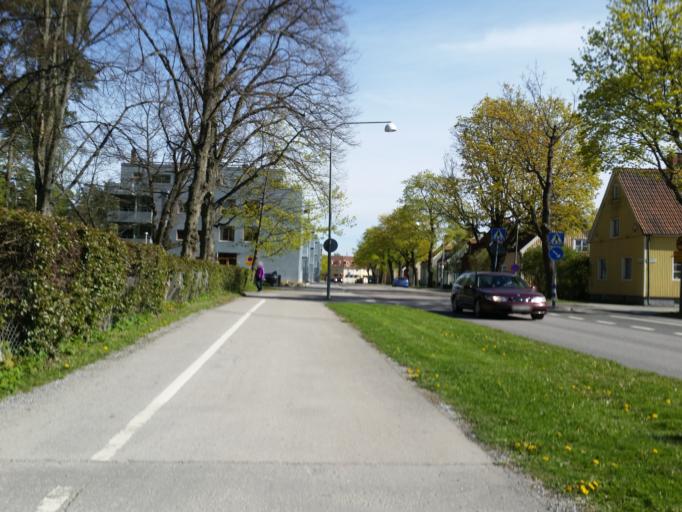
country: SE
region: Stockholm
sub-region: Stockholms Kommun
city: Arsta
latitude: 59.2817
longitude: 18.1054
